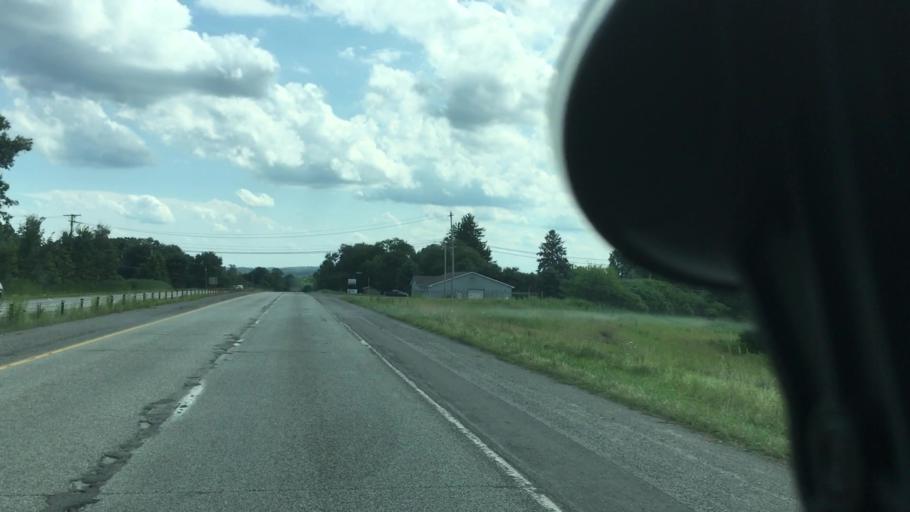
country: US
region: Pennsylvania
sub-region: Mercer County
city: Reynolds Heights
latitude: 41.3165
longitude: -80.4118
